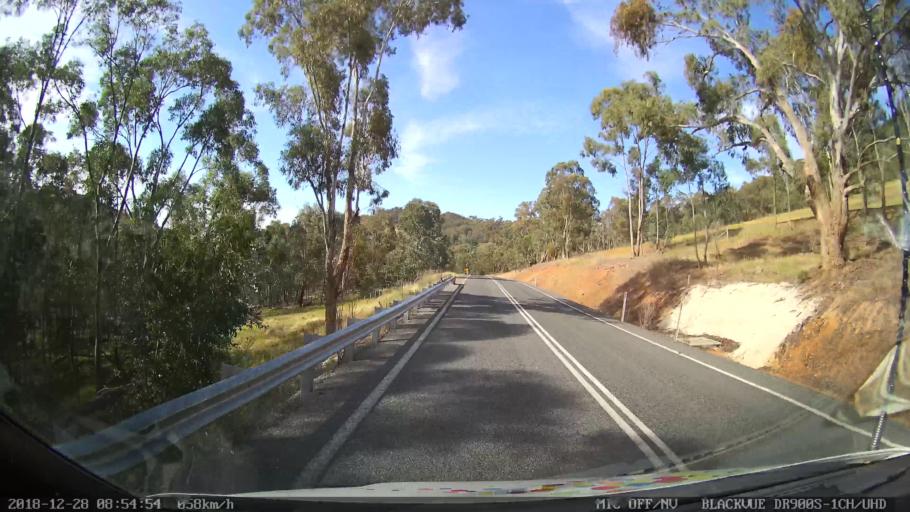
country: AU
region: New South Wales
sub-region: Upper Lachlan Shire
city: Crookwell
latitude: -34.0958
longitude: 149.3324
